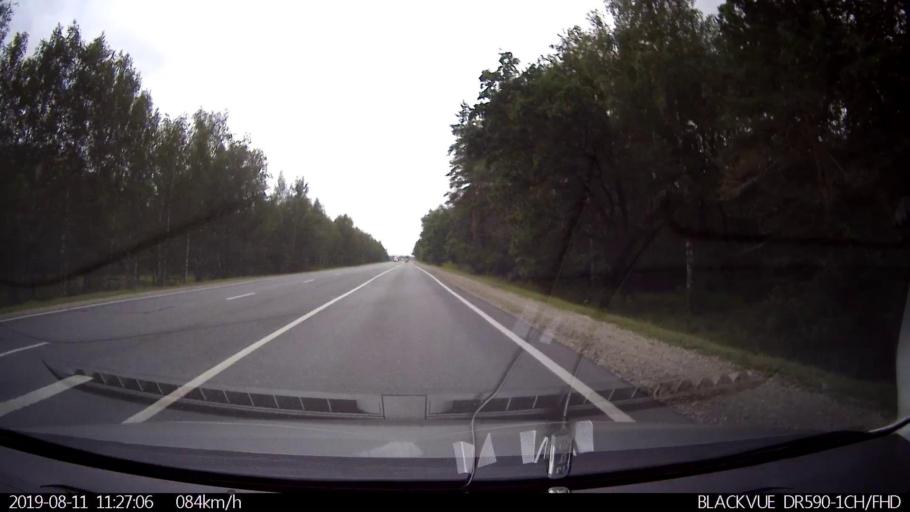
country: RU
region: Ulyanovsk
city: Krasnyy Gulyay
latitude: 54.0972
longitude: 48.2328
